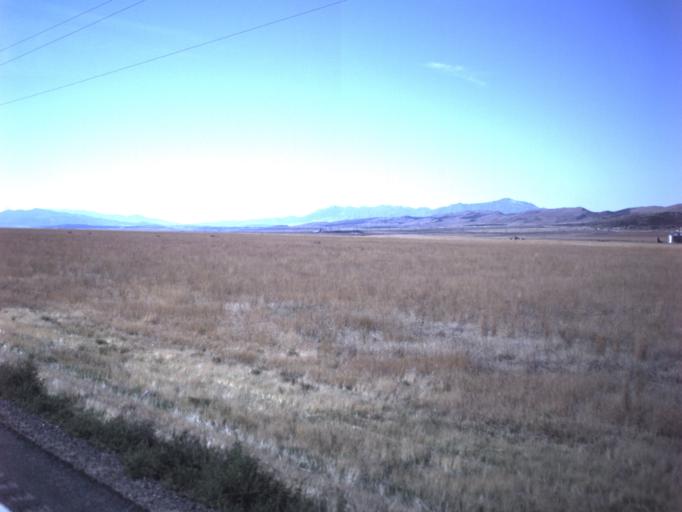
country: US
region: Utah
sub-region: Juab County
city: Nephi
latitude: 39.6271
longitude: -111.8618
